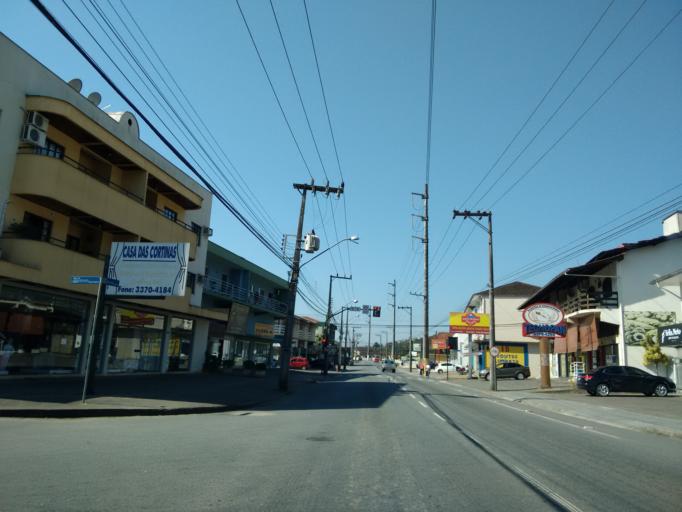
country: BR
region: Santa Catarina
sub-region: Jaragua Do Sul
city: Jaragua do Sul
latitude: -26.4913
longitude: -49.0623
